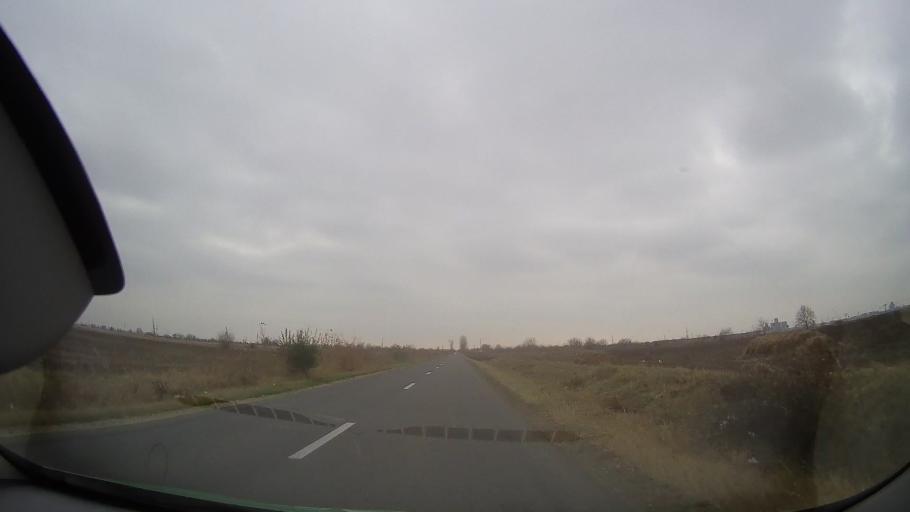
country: RO
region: Ialomita
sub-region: Comuna Manasia
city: Manasia
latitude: 44.7198
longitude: 26.6854
